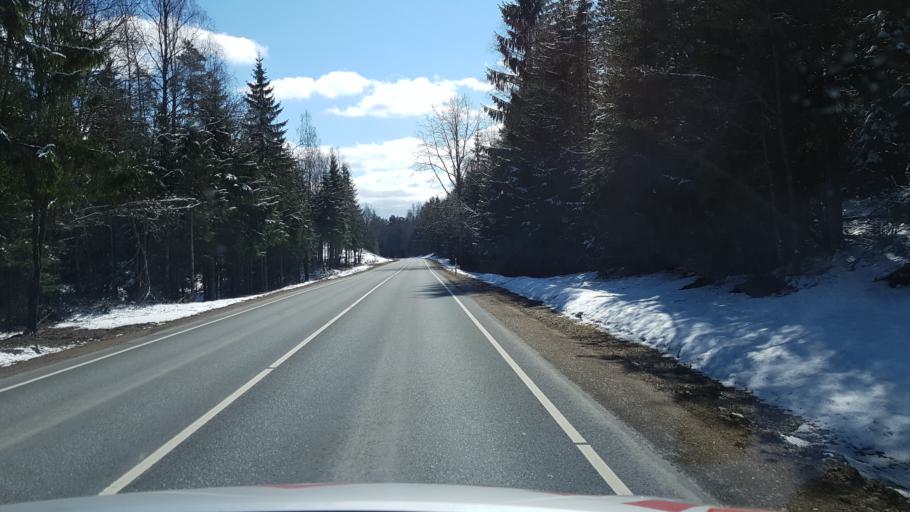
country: EE
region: Laeaene-Virumaa
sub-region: Tapa vald
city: Tapa
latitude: 59.4087
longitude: 26.0021
